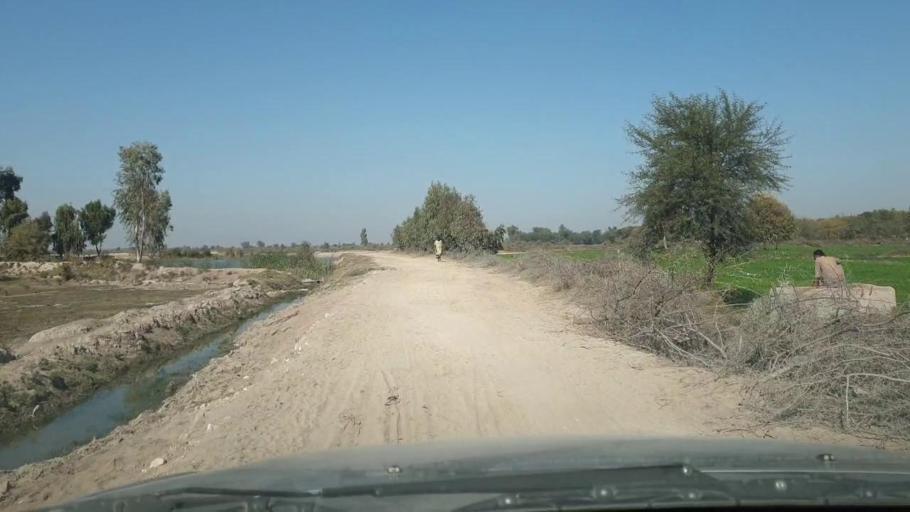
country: PK
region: Sindh
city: Adilpur
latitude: 27.8927
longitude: 69.2555
